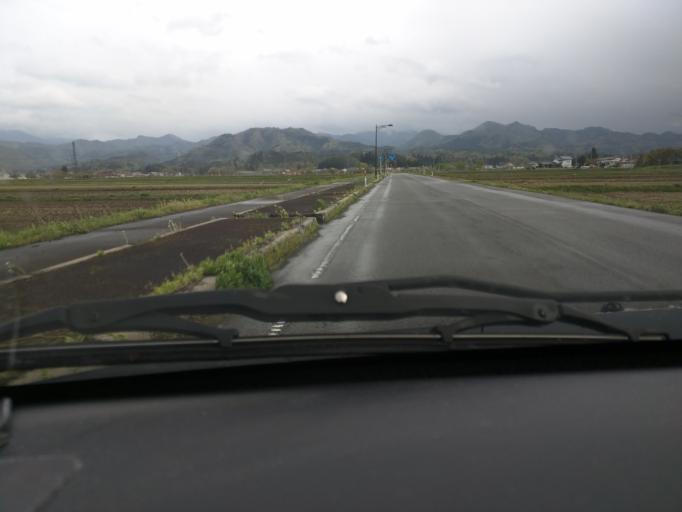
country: JP
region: Fukushima
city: Kitakata
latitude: 37.4489
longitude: 139.8554
